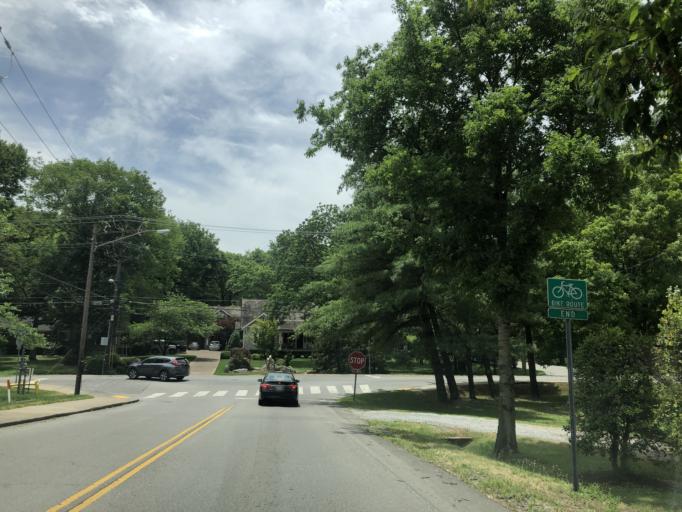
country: US
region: Tennessee
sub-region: Davidson County
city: Oak Hill
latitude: 36.1017
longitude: -86.8020
